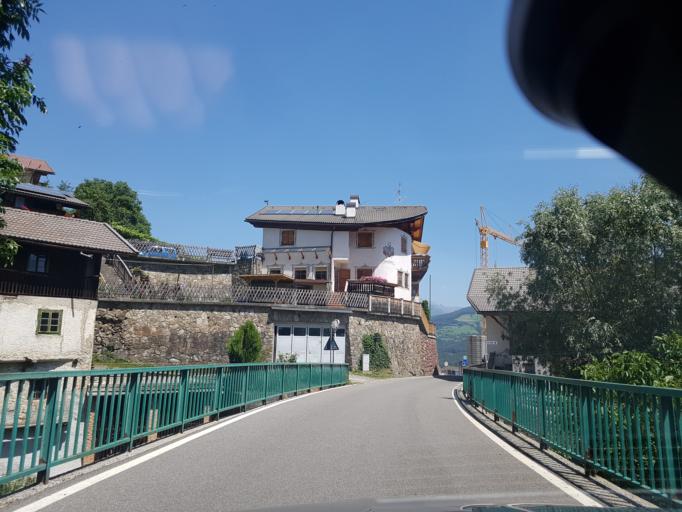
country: IT
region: Trentino-Alto Adige
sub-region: Bolzano
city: Villandro - Villanders
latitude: 46.6290
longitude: 11.5333
